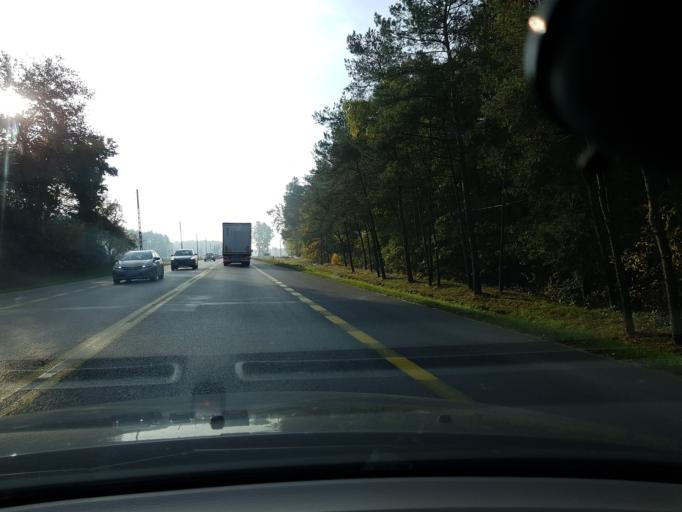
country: PL
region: Masovian Voivodeship
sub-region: Powiat otwocki
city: Otwock
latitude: 52.1470
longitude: 21.3219
